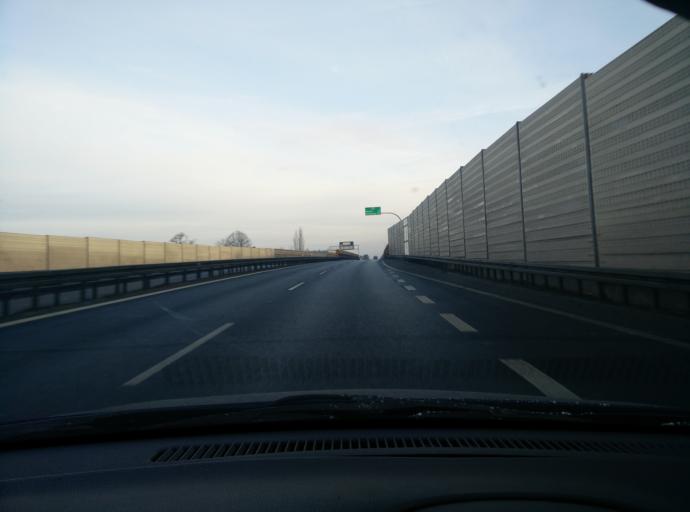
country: PL
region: Greater Poland Voivodeship
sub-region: Powiat poznanski
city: Kornik
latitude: 52.2993
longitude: 17.0494
